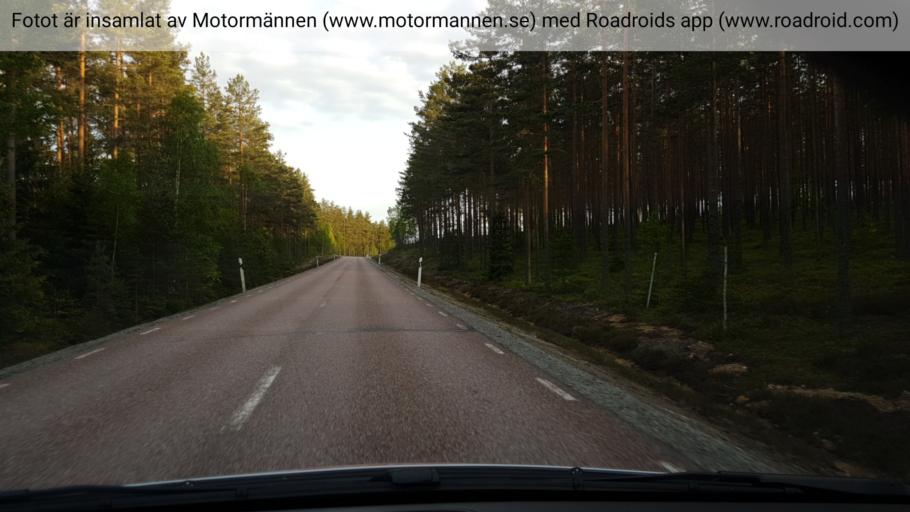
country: SE
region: Vaestmanland
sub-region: Skinnskattebergs Kommun
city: Skinnskatteberg
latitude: 59.8106
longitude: 15.8407
